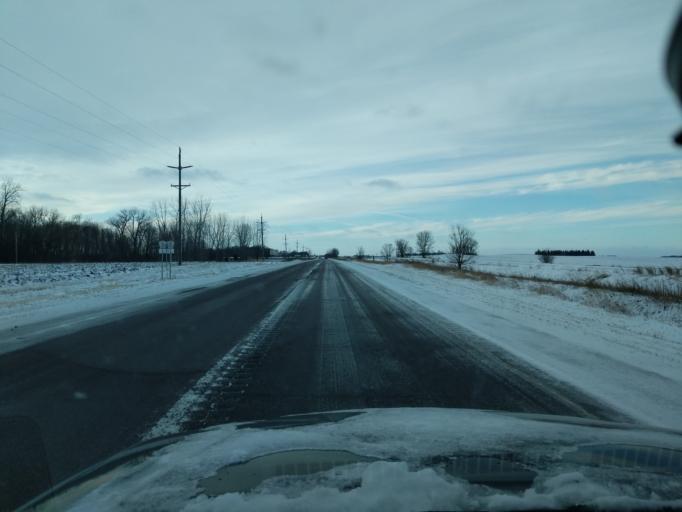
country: US
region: Minnesota
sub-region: Renville County
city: Hector
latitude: 44.7240
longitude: -94.5195
